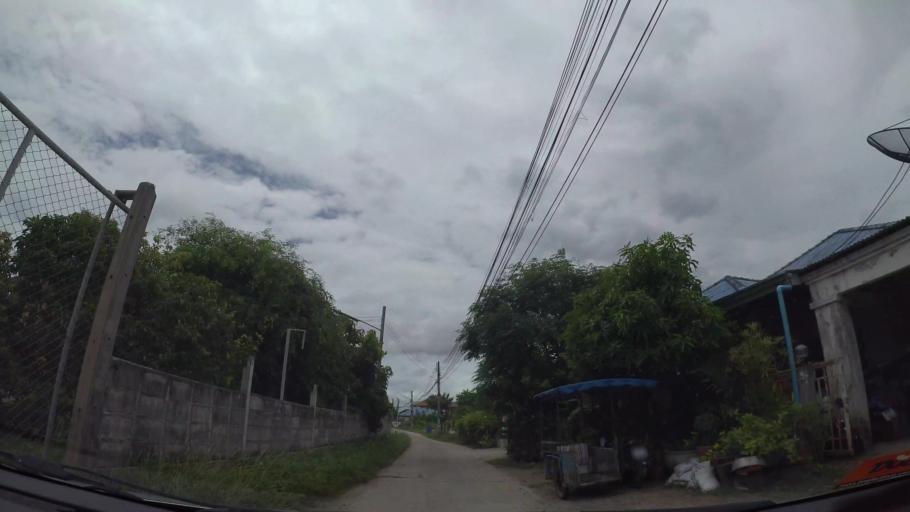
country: TH
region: Chon Buri
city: Sattahip
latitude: 12.7574
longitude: 100.8915
